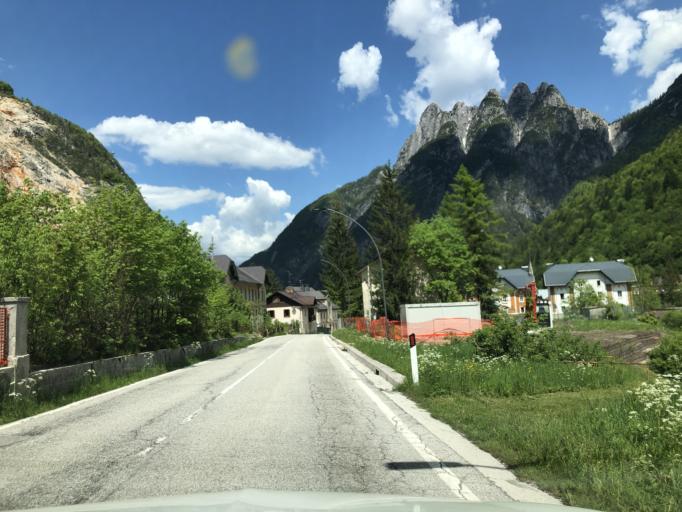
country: IT
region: Friuli Venezia Giulia
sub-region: Provincia di Udine
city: Tarvisio
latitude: 46.4378
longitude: 13.5683
